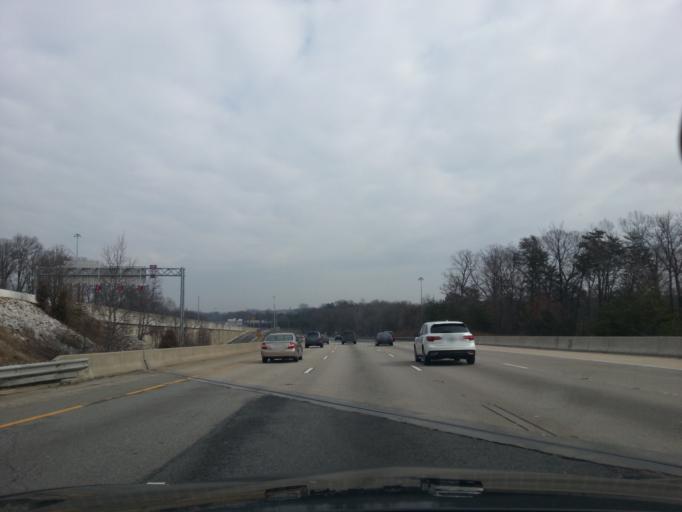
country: US
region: Virginia
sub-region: Fairfax County
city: Lorton
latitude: 38.6803
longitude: -77.2306
